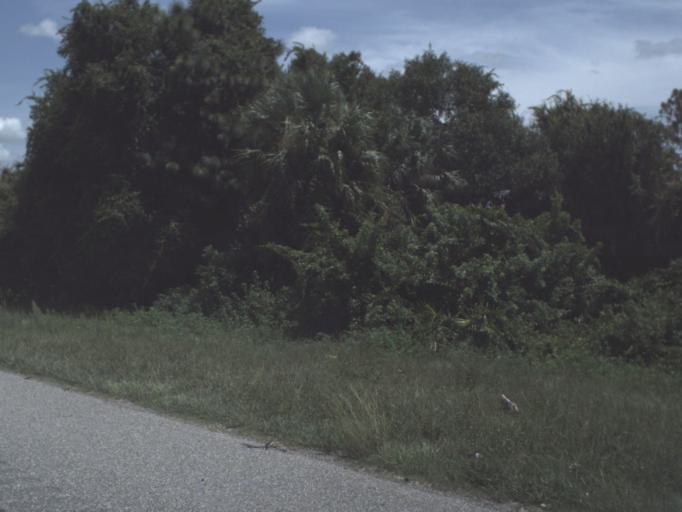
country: US
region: Florida
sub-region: Hillsborough County
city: Gibsonton
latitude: 27.8101
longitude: -82.3520
